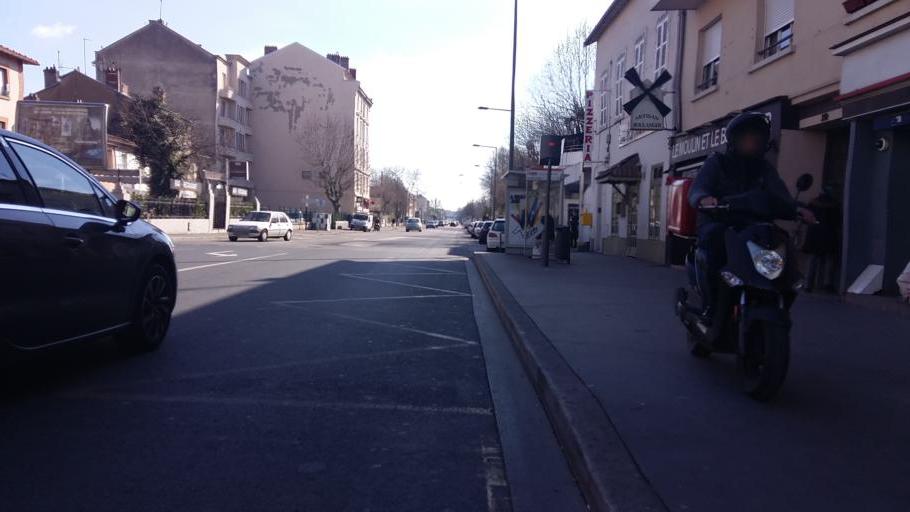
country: FR
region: Rhone-Alpes
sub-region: Departement du Rhone
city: Lyon
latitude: 45.7293
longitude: 4.8537
